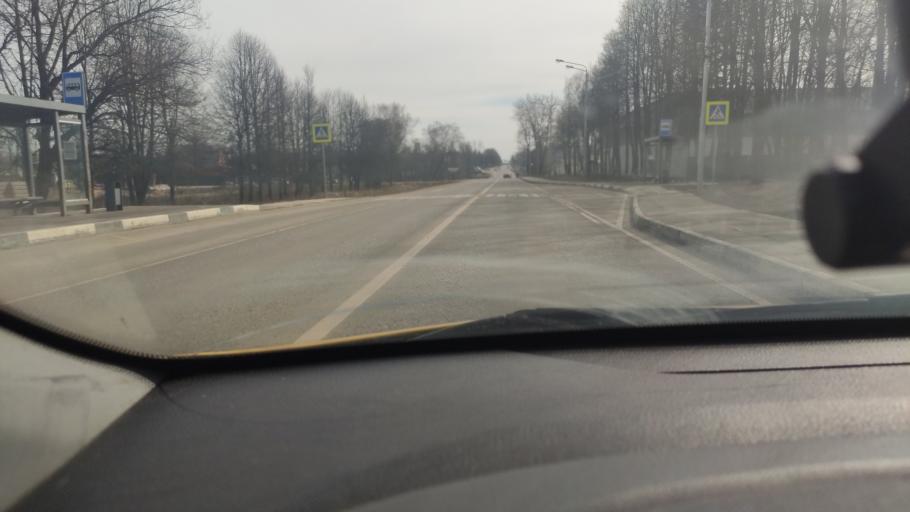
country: RU
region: Moskovskaya
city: Ruza
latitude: 55.7120
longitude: 36.1769
